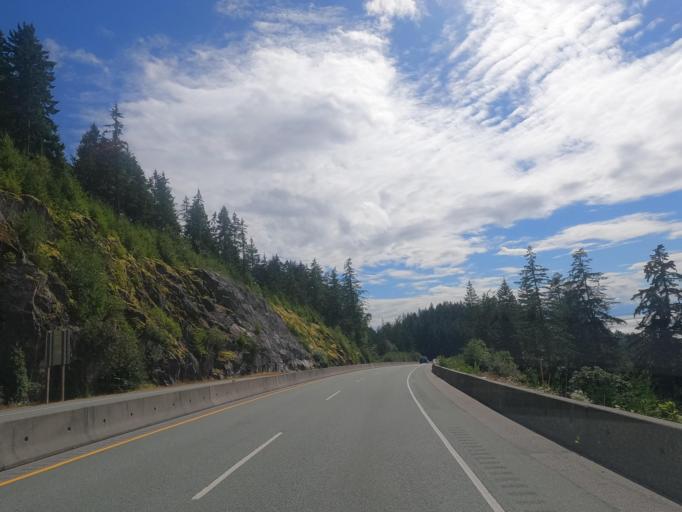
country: CA
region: British Columbia
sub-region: Greater Vancouver Regional District
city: Bowen Island
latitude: 49.3741
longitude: -123.2671
